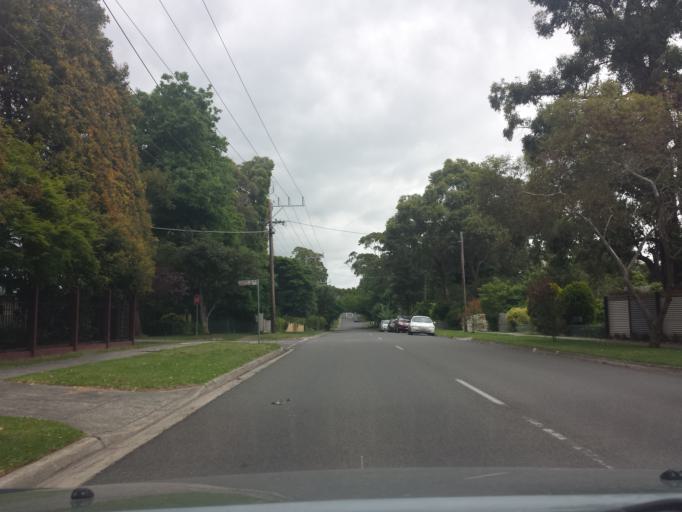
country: AU
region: Victoria
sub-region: Yarra Ranges
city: Belgrave Heights
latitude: -37.9148
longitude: 145.3373
